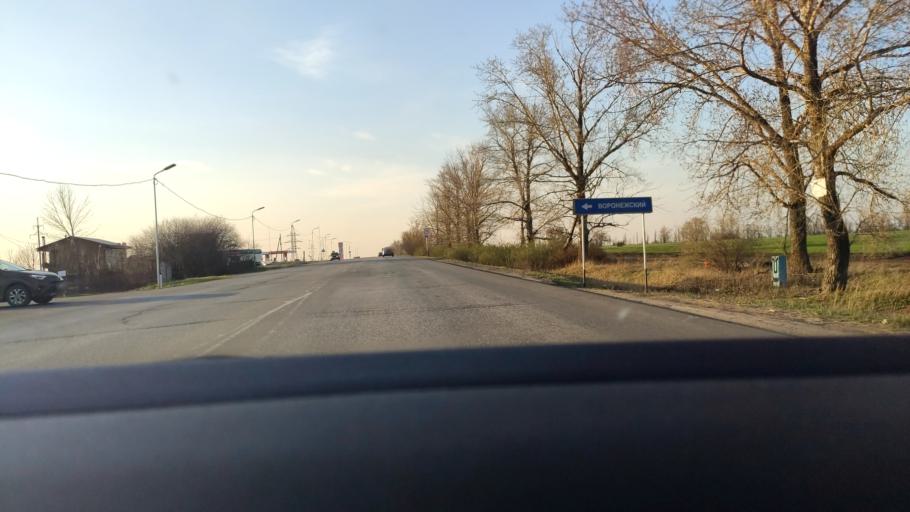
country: RU
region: Voronezj
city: Maslovka
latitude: 51.5044
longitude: 39.3078
